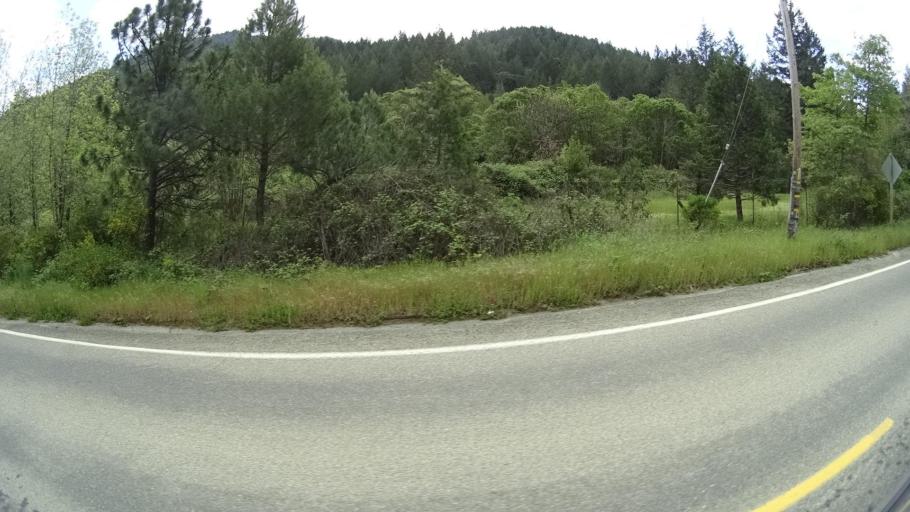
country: US
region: California
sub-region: Humboldt County
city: Redway
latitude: 40.1221
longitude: -123.8816
